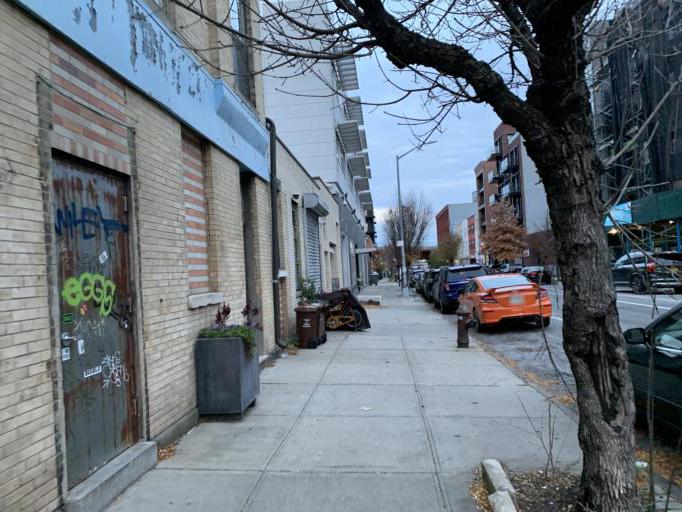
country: US
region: New York
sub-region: Queens County
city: Long Island City
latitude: 40.7374
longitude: -73.9552
